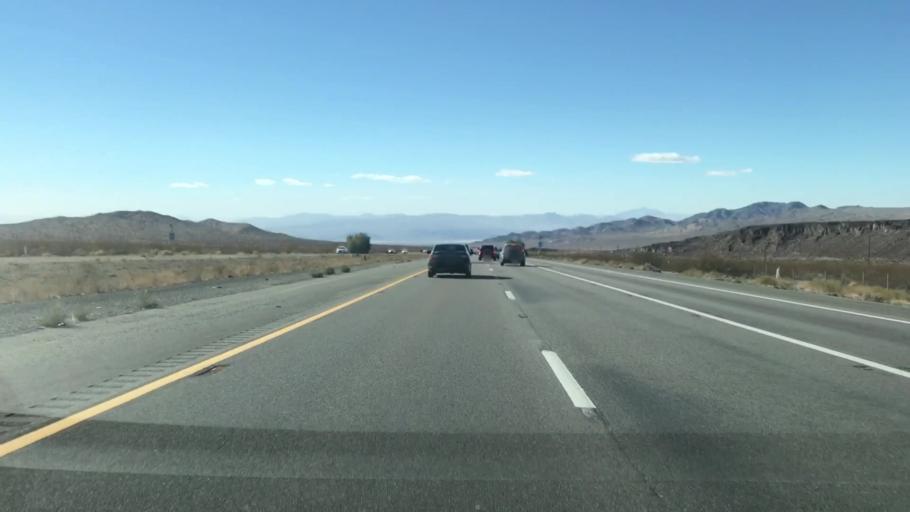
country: US
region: Nevada
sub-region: Clark County
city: Sandy Valley
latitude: 35.3847
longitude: -115.8592
